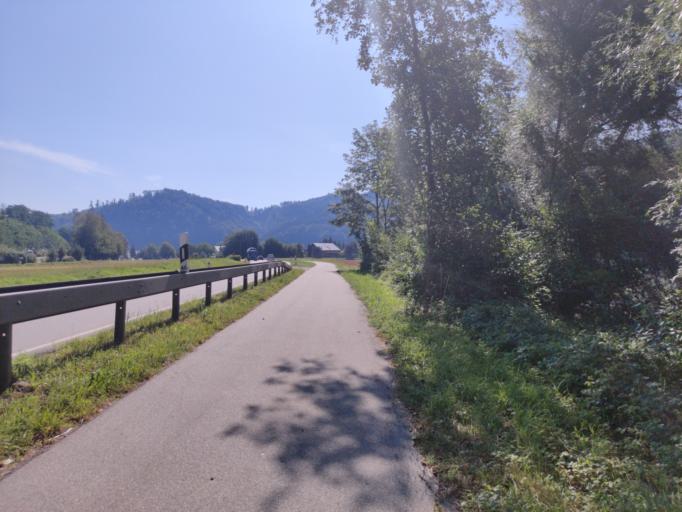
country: DE
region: Bavaria
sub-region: Lower Bavaria
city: Thyrnau
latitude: 48.5630
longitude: 13.5691
